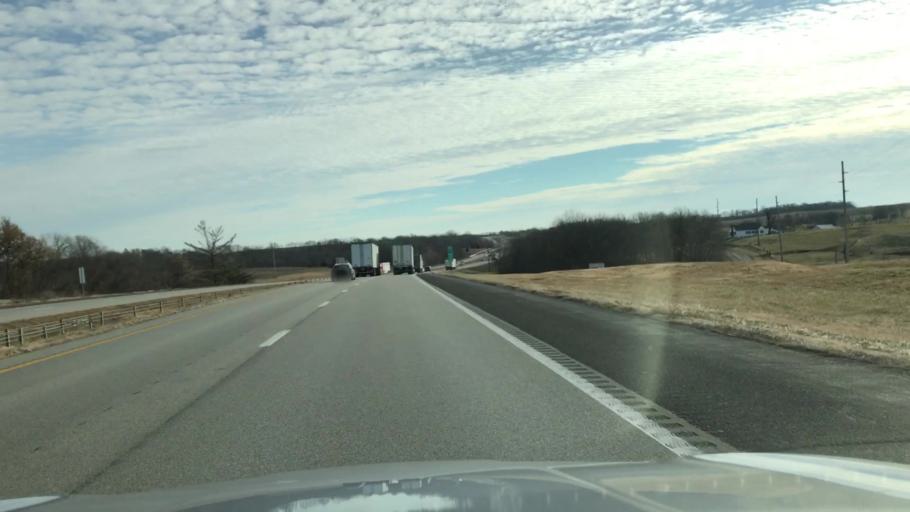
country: US
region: Missouri
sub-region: Lafayette County
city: Concordia
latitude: 38.9916
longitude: -93.6540
